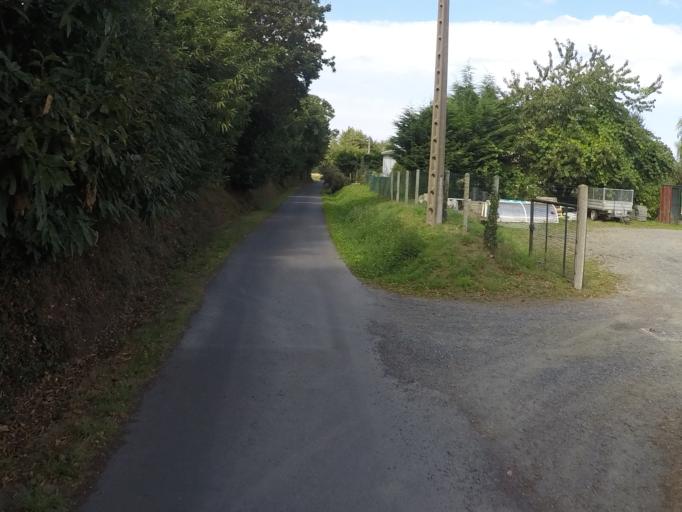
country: FR
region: Brittany
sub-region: Departement des Cotes-d'Armor
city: Goudelin
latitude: 48.6102
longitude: -3.0090
